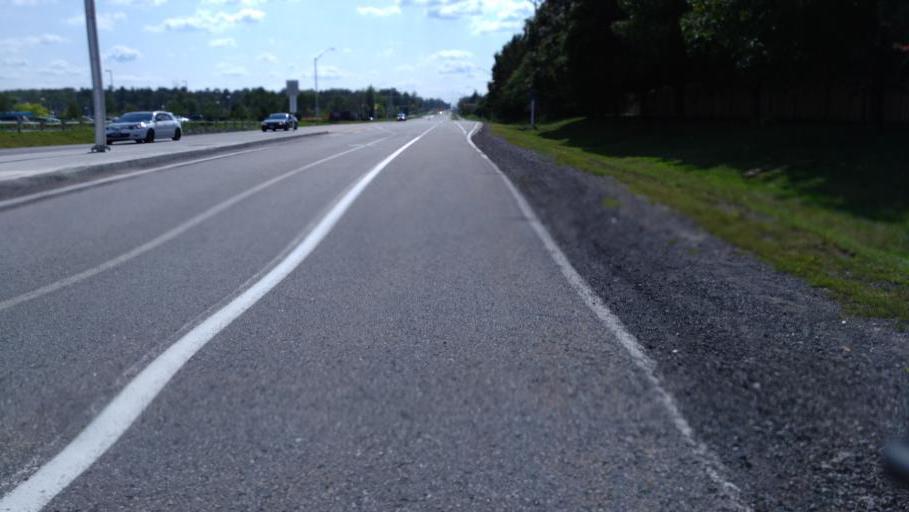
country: CA
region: Ontario
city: Bells Corners
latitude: 45.3465
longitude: -75.9289
